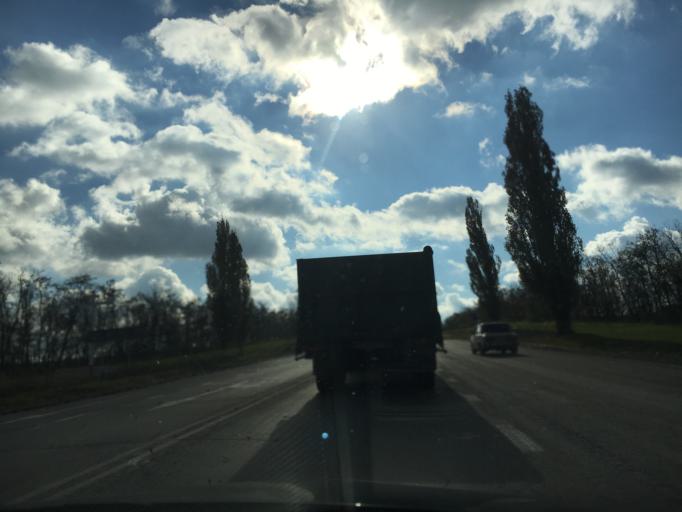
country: RU
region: Rostov
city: Matveyev Kurgan
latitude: 47.5445
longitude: 38.8910
